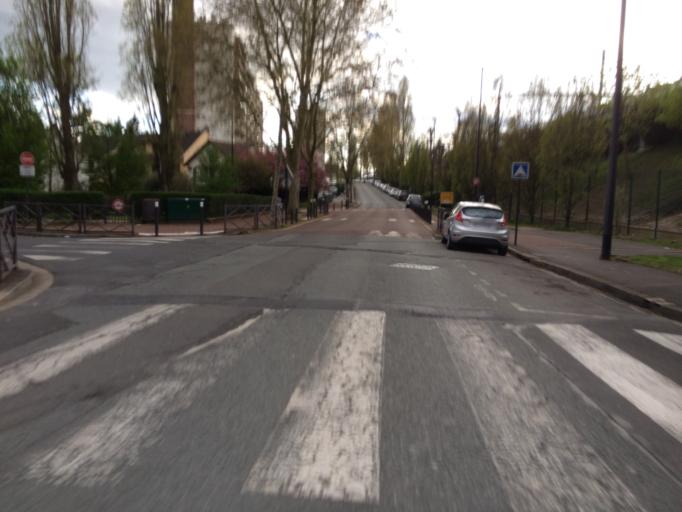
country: FR
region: Ile-de-France
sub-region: Departement des Hauts-de-Seine
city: Antony
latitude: 48.7614
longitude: 2.3047
